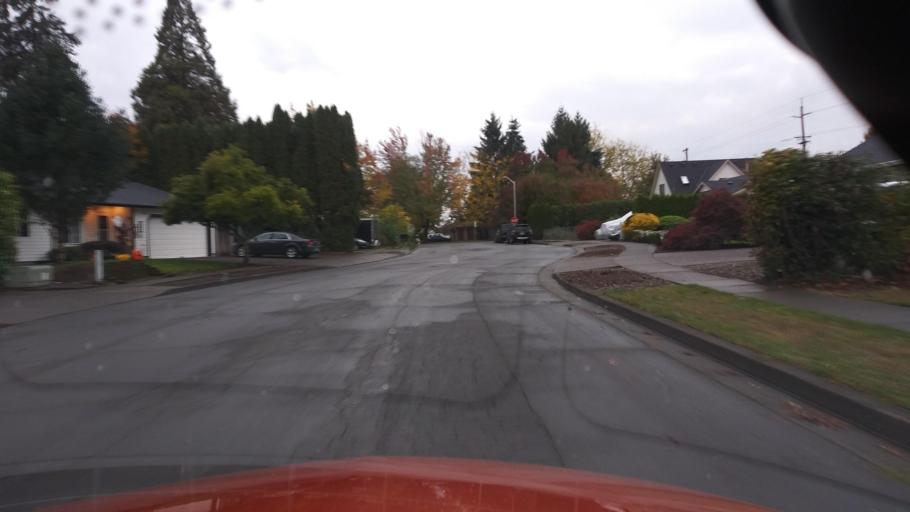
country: US
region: Oregon
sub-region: Washington County
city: Cornelius
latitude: 45.5238
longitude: -123.0346
